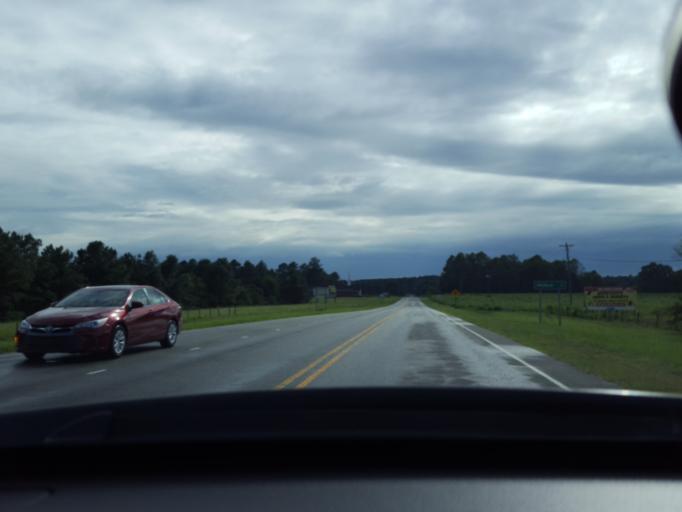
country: US
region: North Carolina
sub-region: Duplin County
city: Kenansville
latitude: 34.9169
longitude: -78.0258
